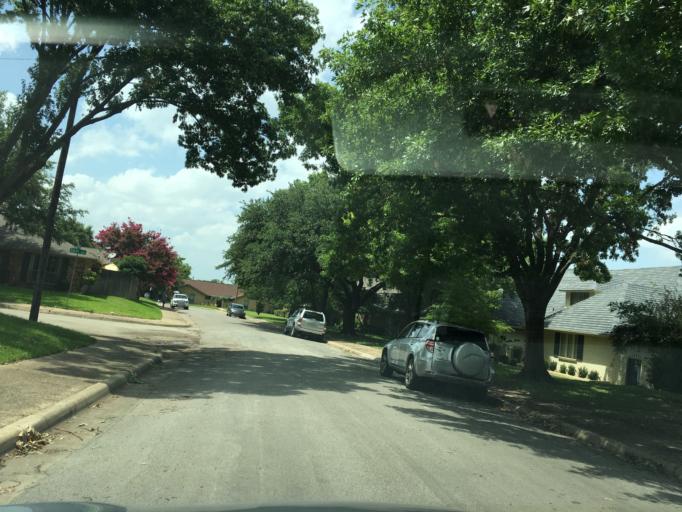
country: US
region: Texas
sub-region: Dallas County
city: University Park
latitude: 32.8905
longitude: -96.7781
